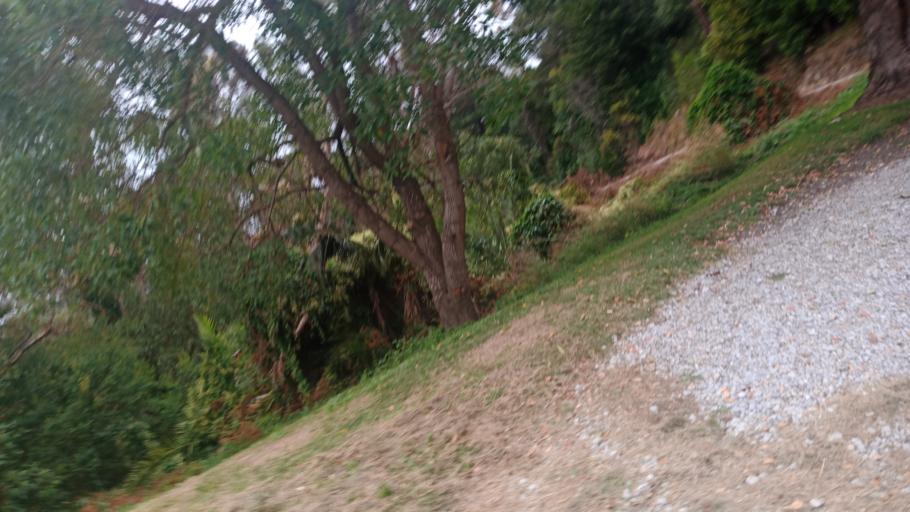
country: NZ
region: Gisborne
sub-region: Gisborne District
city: Gisborne
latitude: -38.6743
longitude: 178.0294
